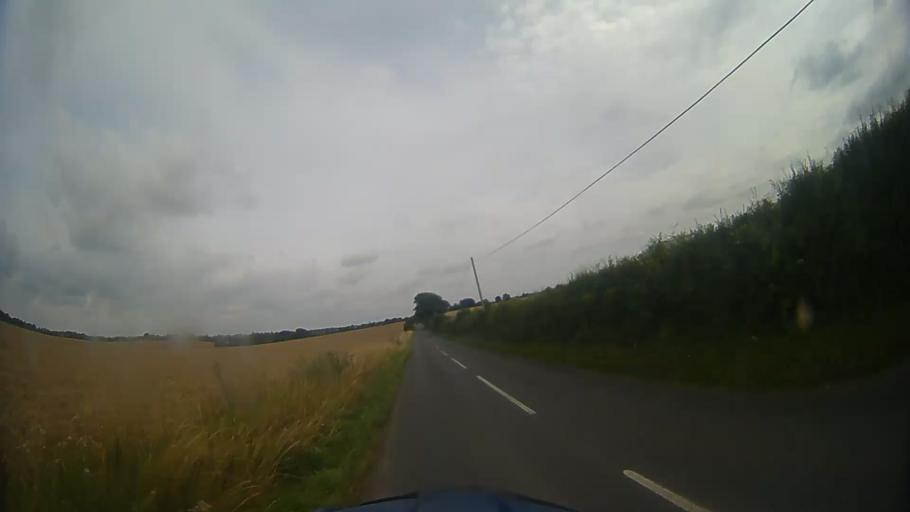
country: GB
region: England
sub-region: Hampshire
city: Basingstoke
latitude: 51.2539
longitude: -1.1471
